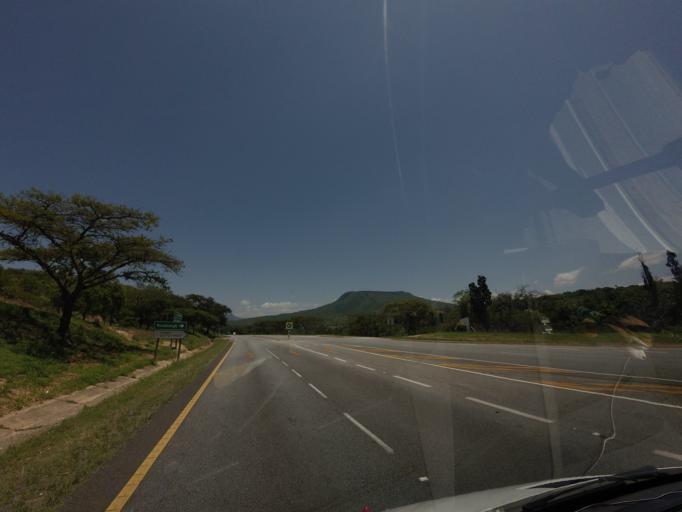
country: ZA
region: Mpumalanga
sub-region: Ehlanzeni District
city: Nelspruit
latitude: -25.4285
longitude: 30.7861
